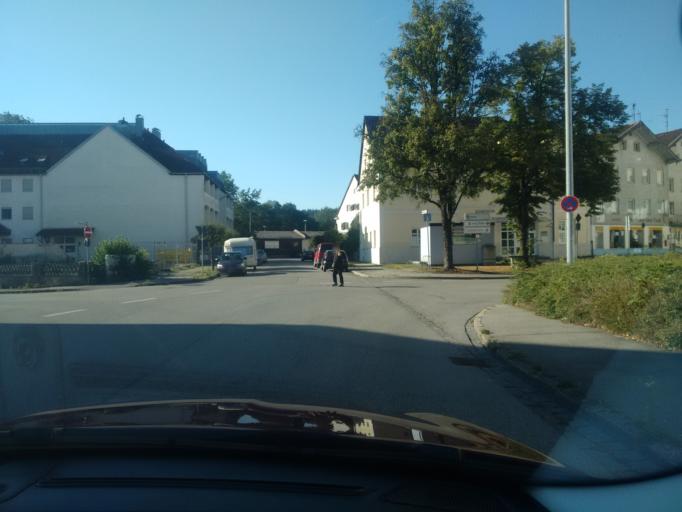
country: DE
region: Bavaria
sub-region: Upper Bavaria
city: Trostberg an der Alz
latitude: 48.0259
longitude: 12.5551
